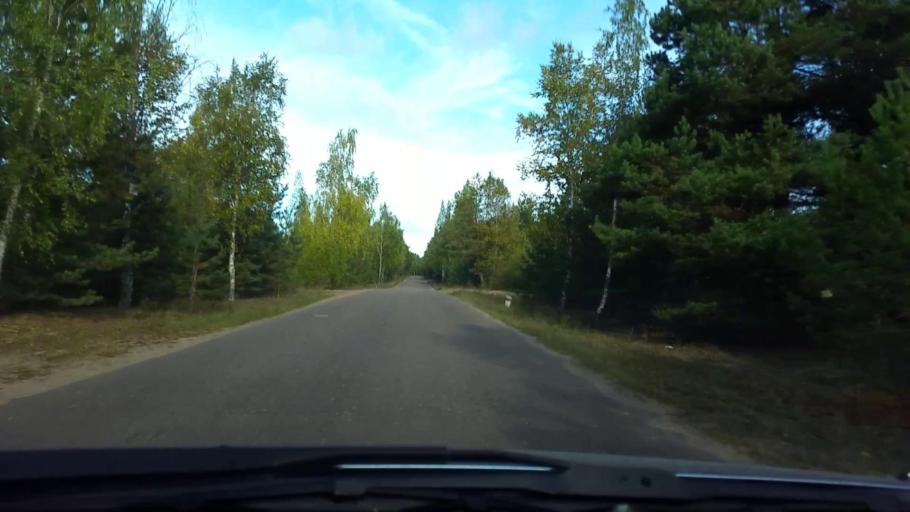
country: LV
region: Adazi
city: Adazi
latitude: 57.1095
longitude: 24.3648
